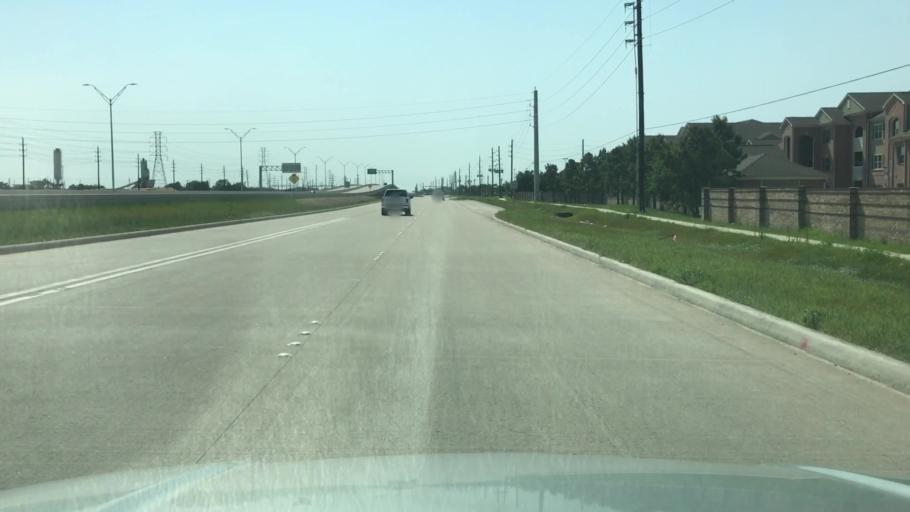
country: US
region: Texas
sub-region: Fort Bend County
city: Cinco Ranch
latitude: 29.6984
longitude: -95.8063
